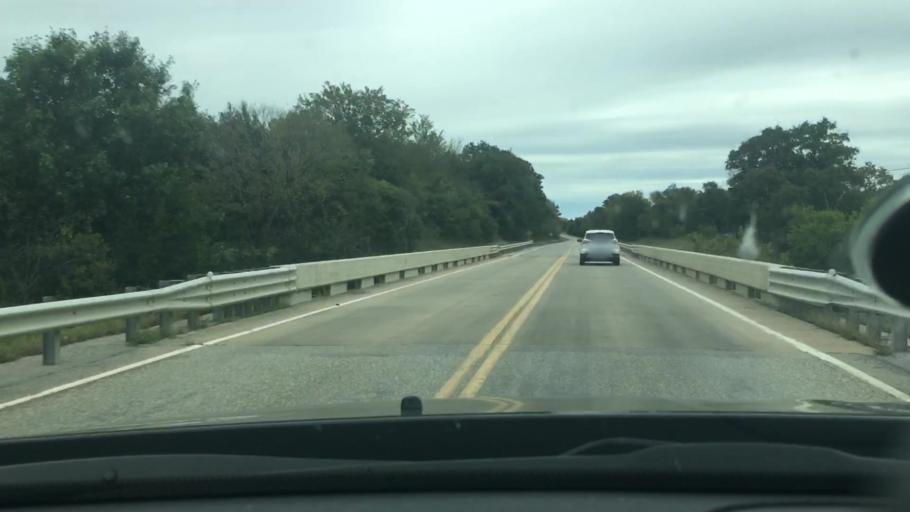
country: US
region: Oklahoma
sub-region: Johnston County
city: Tishomingo
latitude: 34.3289
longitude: -96.4195
